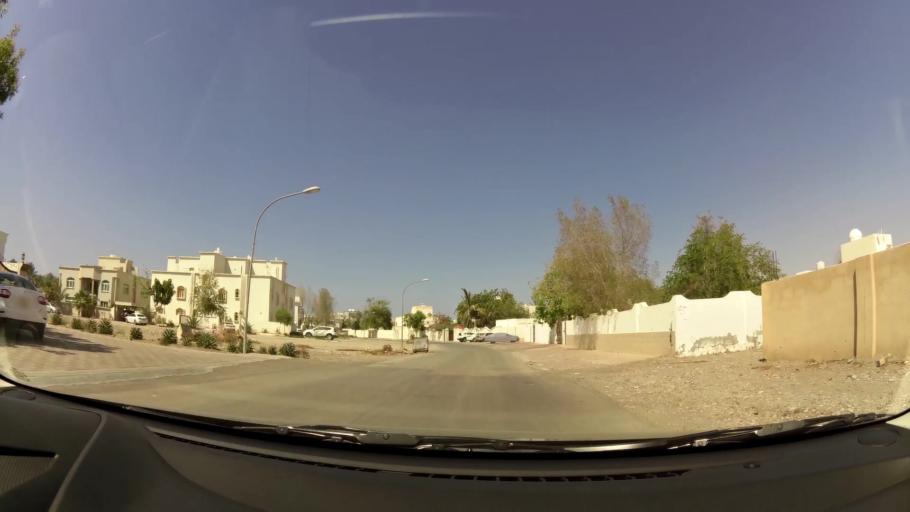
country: OM
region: Muhafazat Masqat
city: As Sib al Jadidah
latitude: 23.6346
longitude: 58.2204
